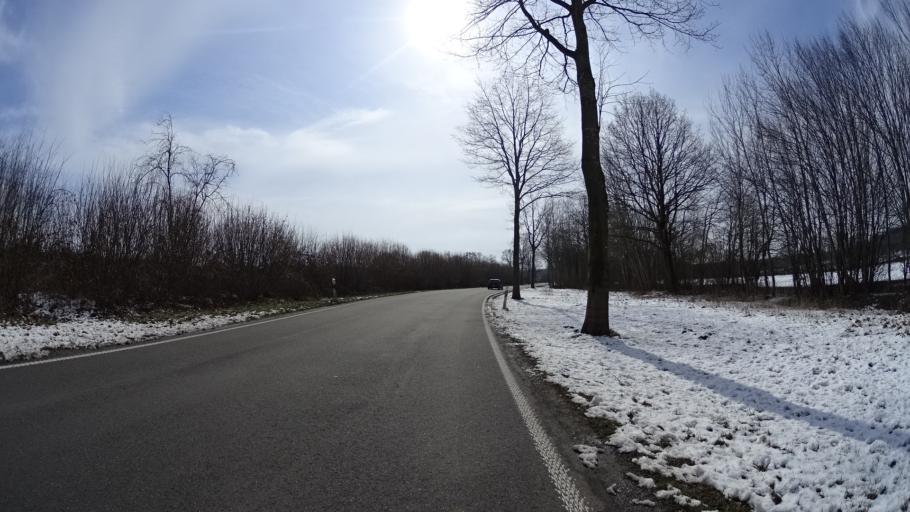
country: DE
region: Schleswig-Holstein
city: Latendorf
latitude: 54.0090
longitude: 10.0606
